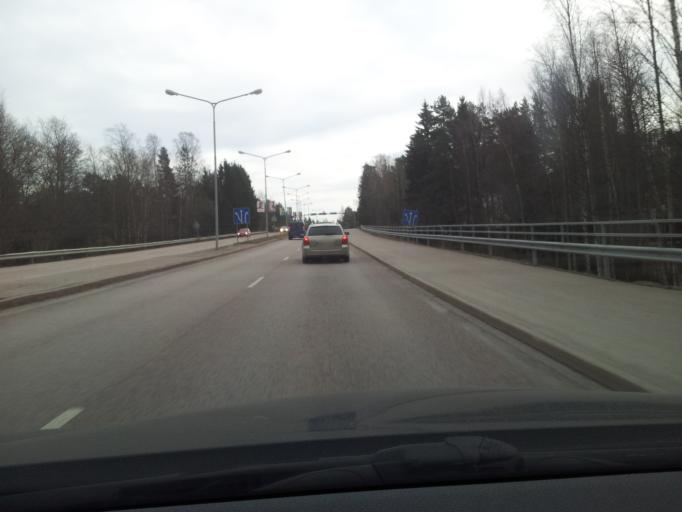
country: FI
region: Uusimaa
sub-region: Helsinki
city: Espoo
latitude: 60.1458
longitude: 24.6727
